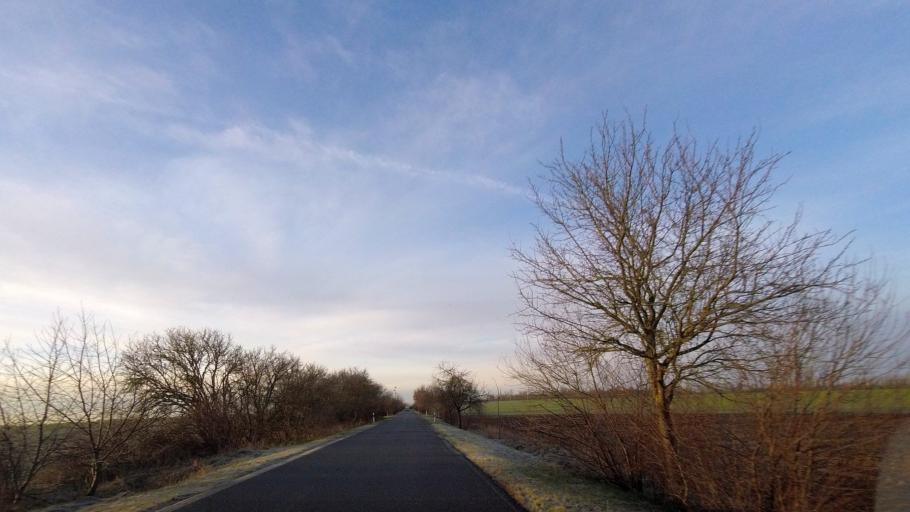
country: DE
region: Brandenburg
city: Niedergorsdorf
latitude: 51.9791
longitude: 12.9360
